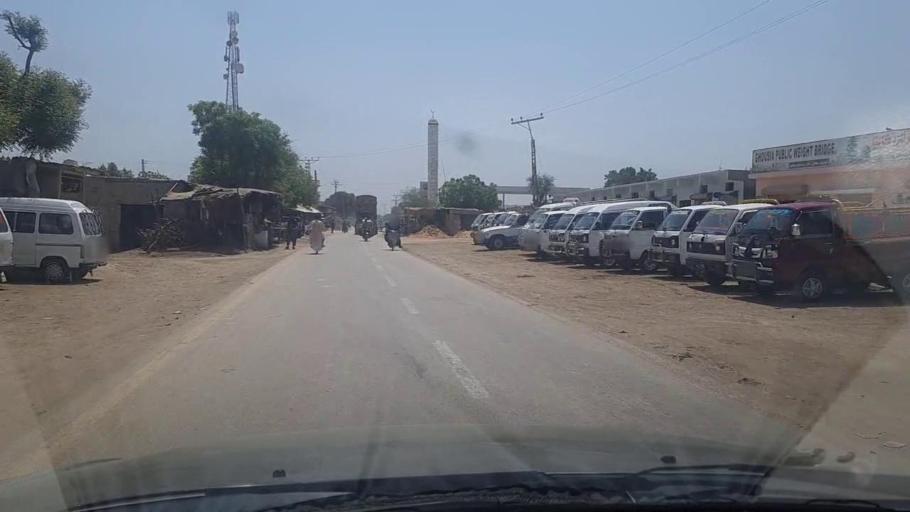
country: PK
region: Sindh
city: Tando Jam
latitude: 25.3567
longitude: 68.4998
